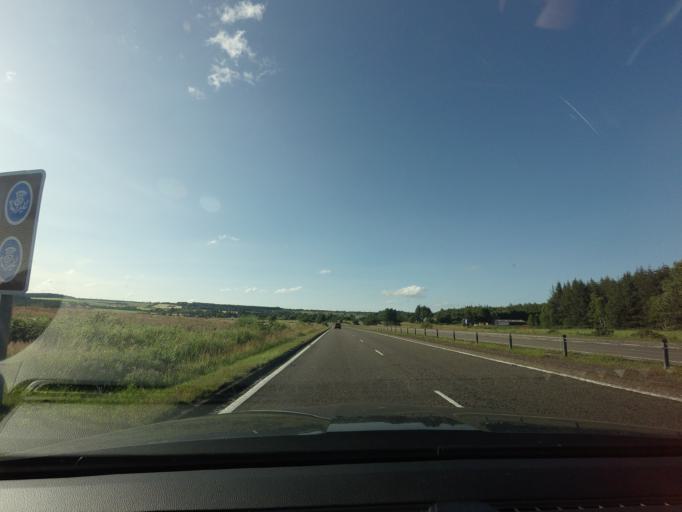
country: GB
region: Scotland
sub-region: Highland
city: Conon Bridge
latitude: 57.5337
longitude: -4.3286
